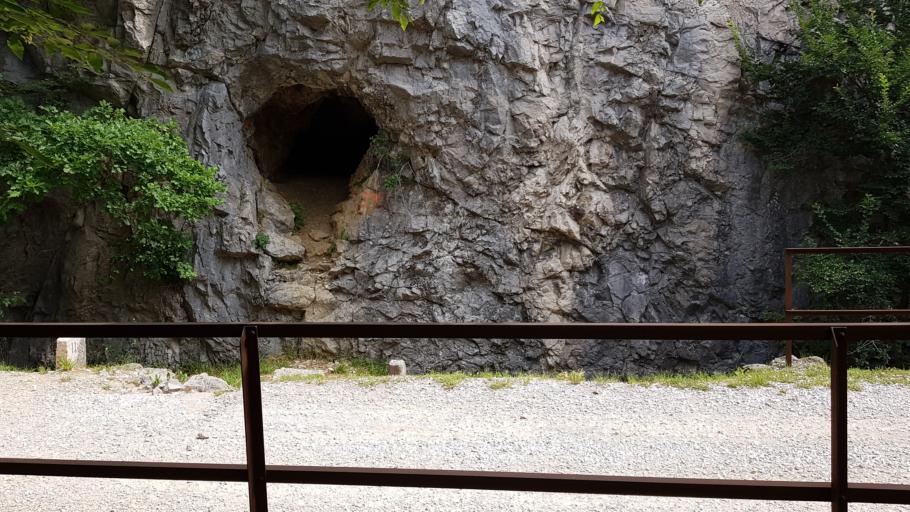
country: IT
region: Friuli Venezia Giulia
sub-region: Provincia di Trieste
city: Dolina
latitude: 45.6210
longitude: 13.8765
